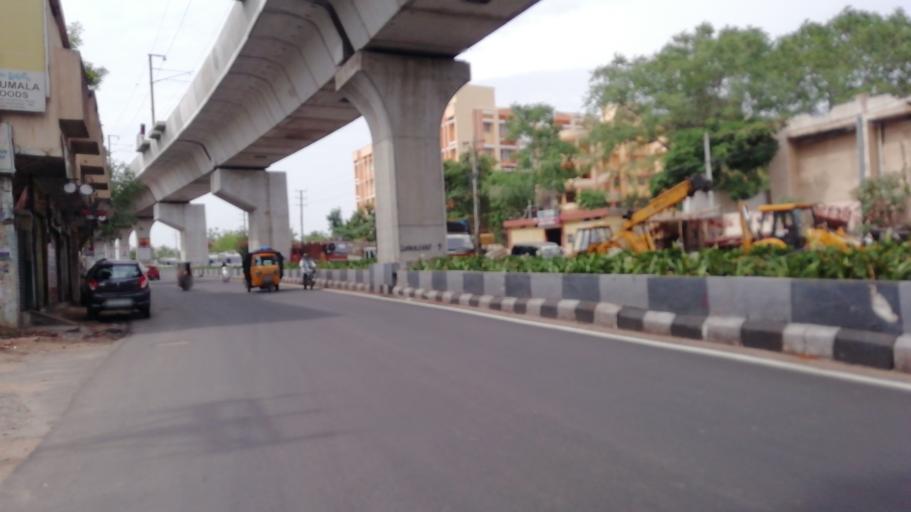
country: IN
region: Telangana
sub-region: Hyderabad
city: Malkajgiri
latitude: 17.4223
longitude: 78.5014
